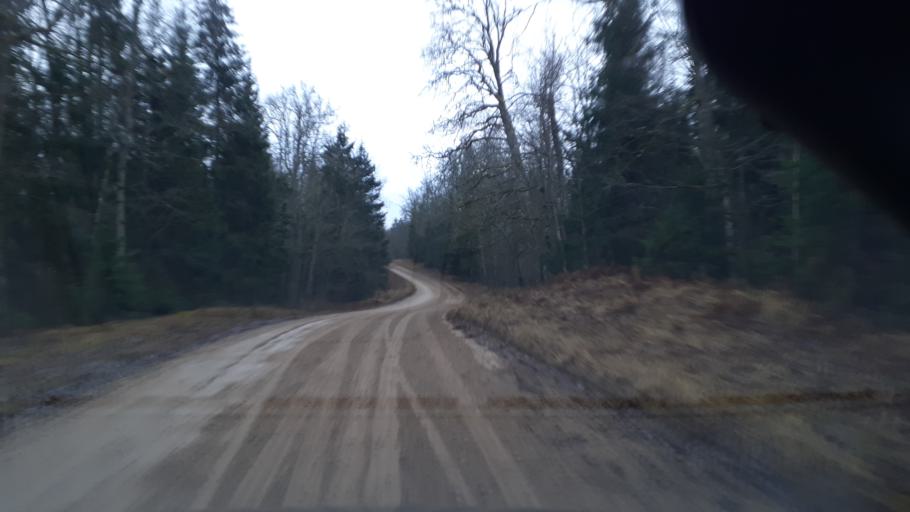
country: LV
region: Kuldigas Rajons
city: Kuldiga
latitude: 56.9230
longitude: 21.7744
